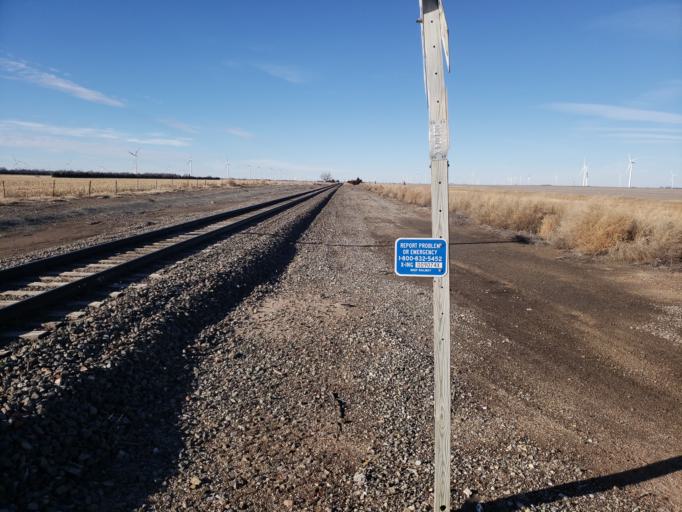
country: US
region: Kansas
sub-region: Edwards County
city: Kinsley
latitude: 37.8852
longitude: -99.5886
